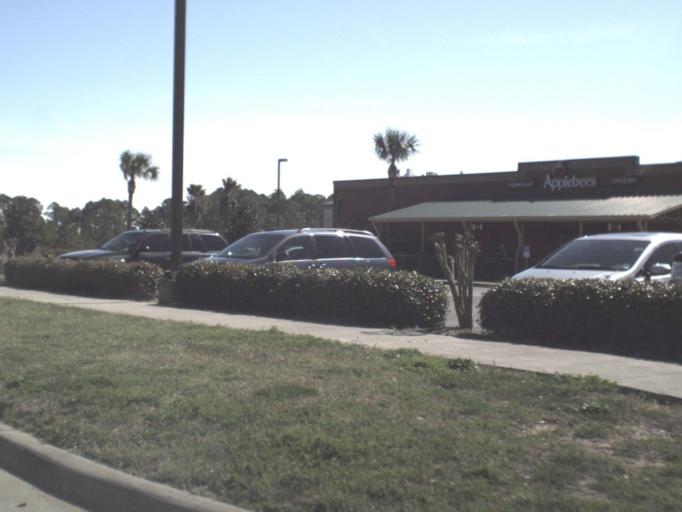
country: US
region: Florida
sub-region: Bay County
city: Panama City Beach
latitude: 30.1839
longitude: -85.8086
